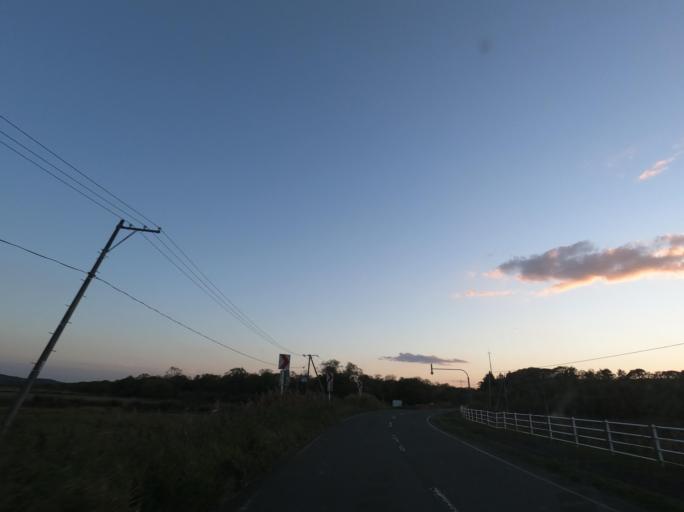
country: JP
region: Hokkaido
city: Kushiro
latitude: 43.2212
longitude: 144.4322
